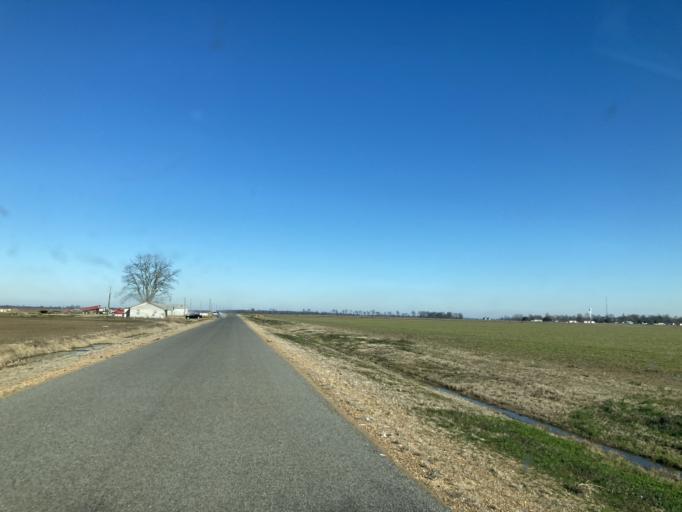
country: US
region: Mississippi
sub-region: Yazoo County
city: Yazoo City
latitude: 32.9681
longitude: -90.6054
